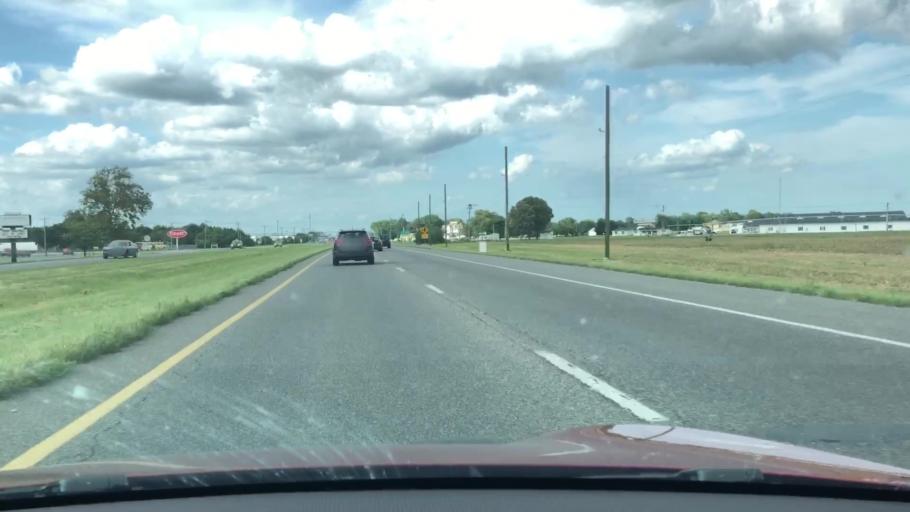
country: US
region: Delaware
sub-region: Sussex County
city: Seaford
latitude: 38.6821
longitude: -75.5913
